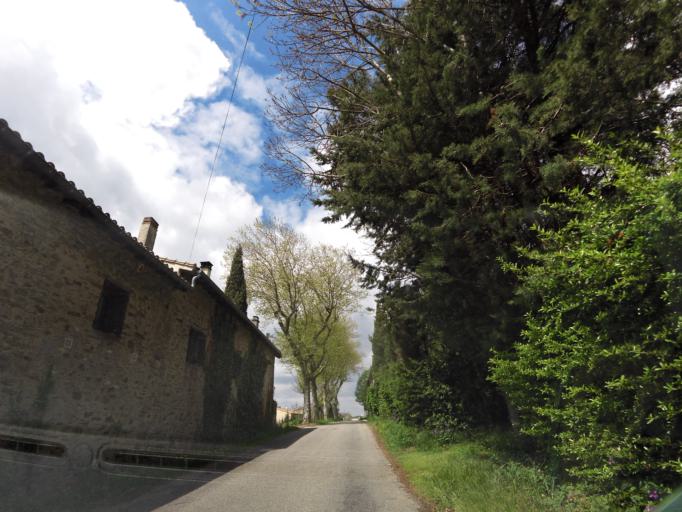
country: FR
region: Languedoc-Roussillon
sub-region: Departement de l'Aude
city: Villepinte
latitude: 43.3532
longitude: 2.1097
